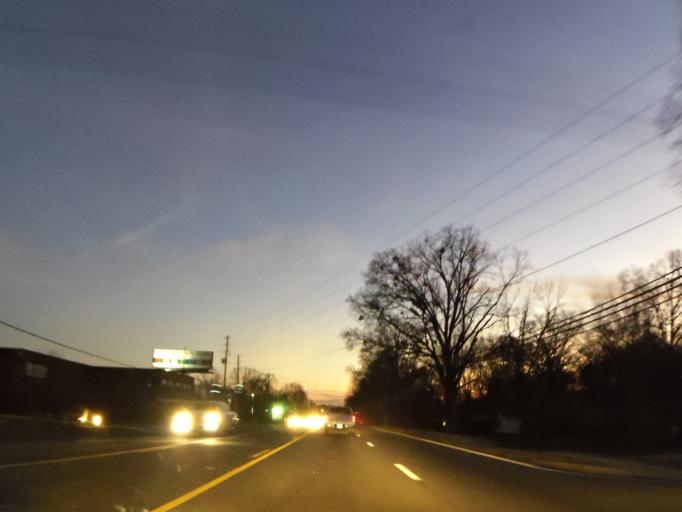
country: US
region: Georgia
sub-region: Whitfield County
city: Dalton
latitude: 34.8210
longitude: -84.9457
